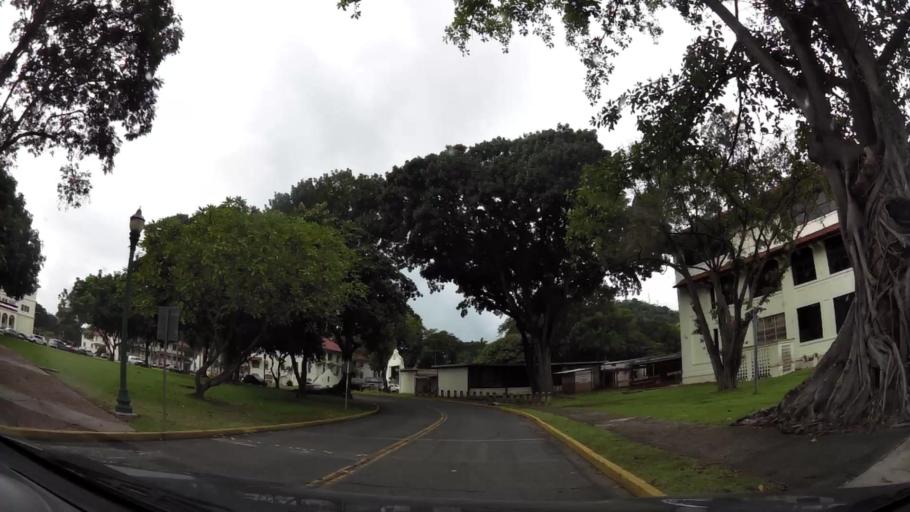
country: PA
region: Panama
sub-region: Distrito de Panama
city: Ancon
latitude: 8.9587
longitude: -79.5566
